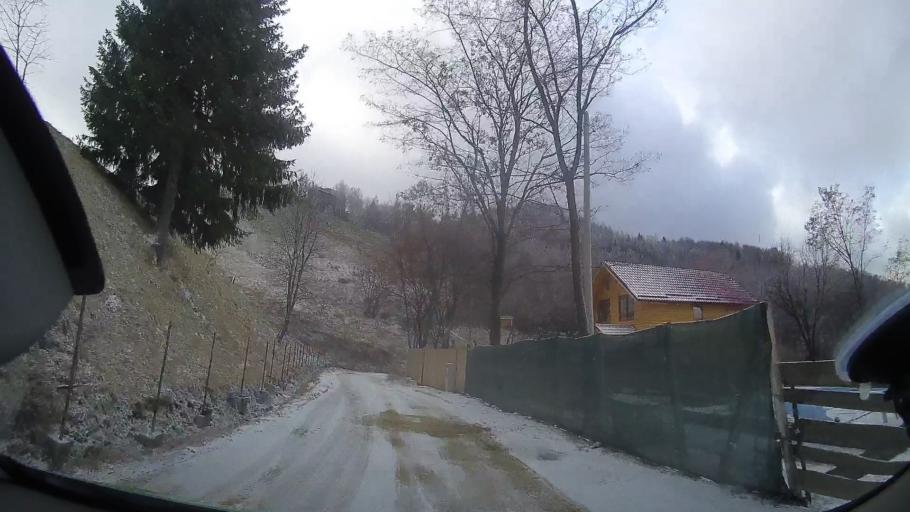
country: RO
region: Cluj
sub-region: Comuna Valea Ierii
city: Valea Ierii
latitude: 46.6657
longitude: 23.3328
